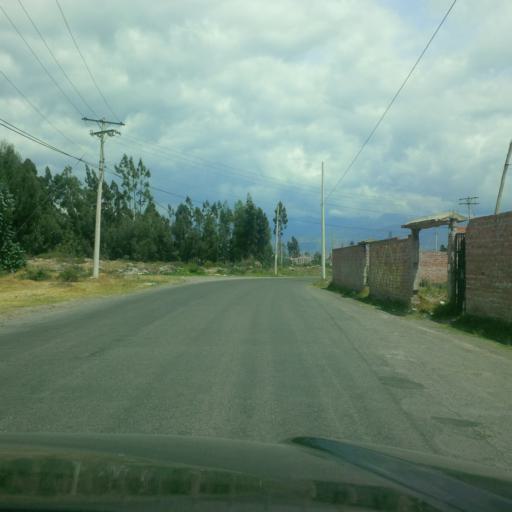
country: EC
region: Chimborazo
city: Riobamba
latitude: -1.6434
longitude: -78.6643
